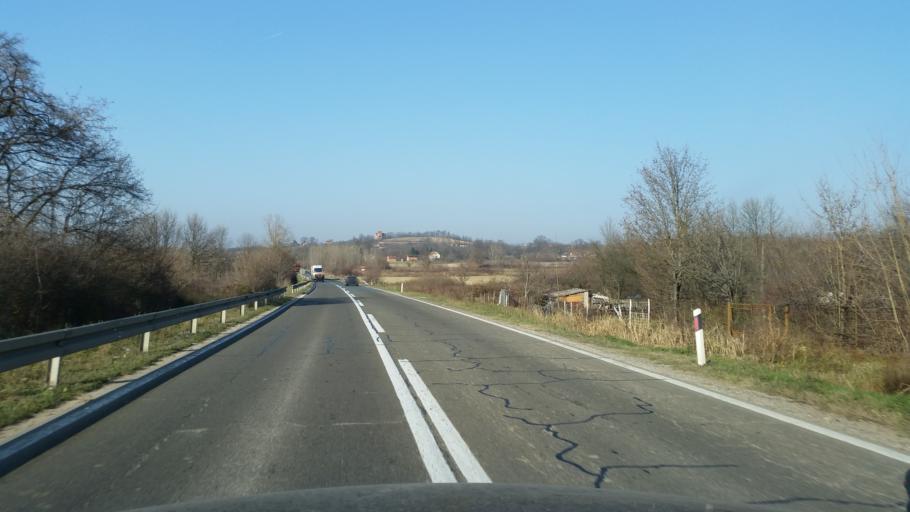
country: RS
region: Central Serbia
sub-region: Kolubarski Okrug
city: Ljig
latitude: 44.2777
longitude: 20.2805
